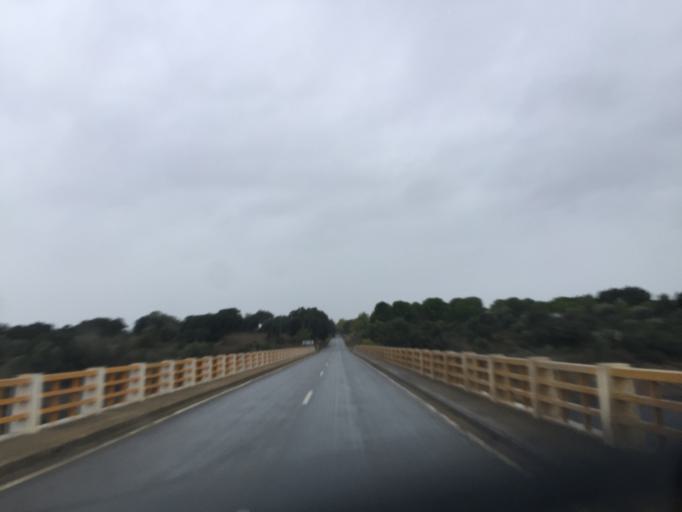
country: PT
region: Portalegre
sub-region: Avis
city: Avis
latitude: 39.0673
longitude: -7.9004
